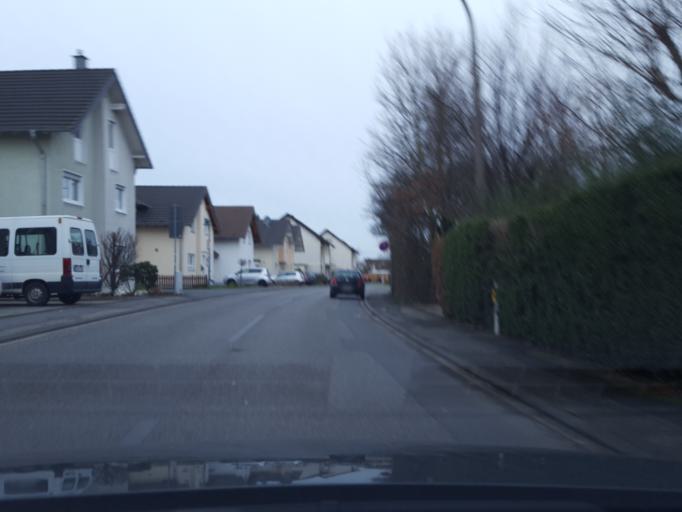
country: DE
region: North Rhine-Westphalia
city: Niederkassel
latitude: 50.7808
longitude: 7.0560
